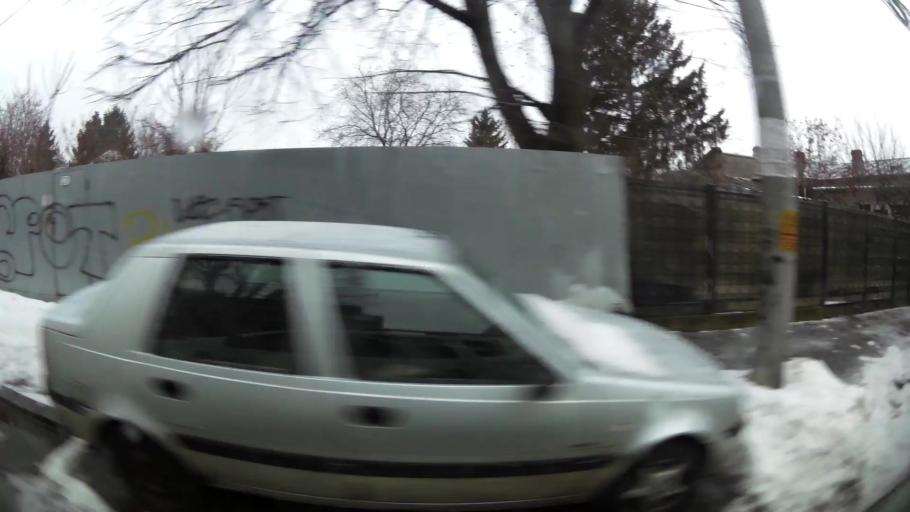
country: RO
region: Ilfov
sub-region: Comuna Chiajna
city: Rosu
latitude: 44.4707
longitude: 26.0472
